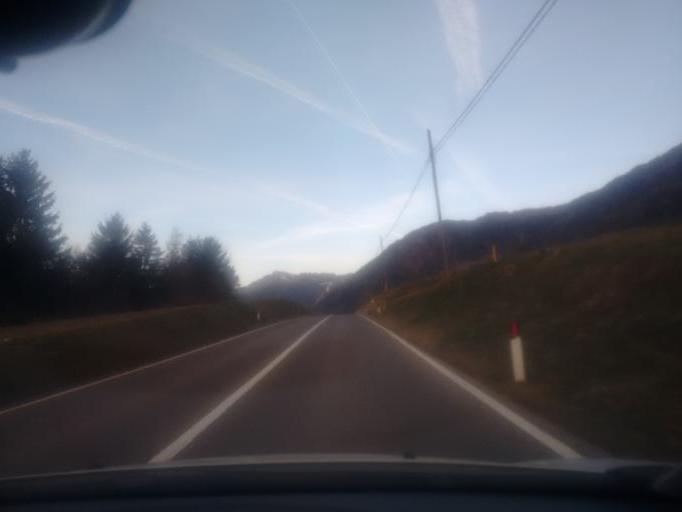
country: IT
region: Trentino-Alto Adige
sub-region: Bolzano
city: Campo di Trens
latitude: 46.8642
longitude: 11.5028
